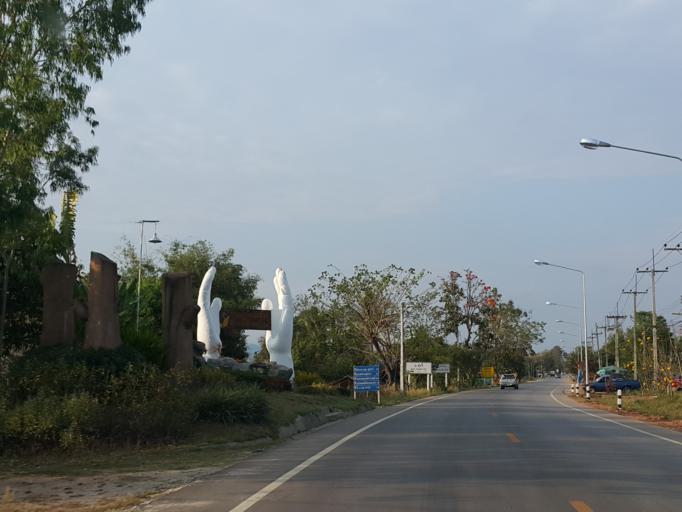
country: TH
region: Lampang
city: Chae Hom
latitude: 18.5278
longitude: 99.4777
